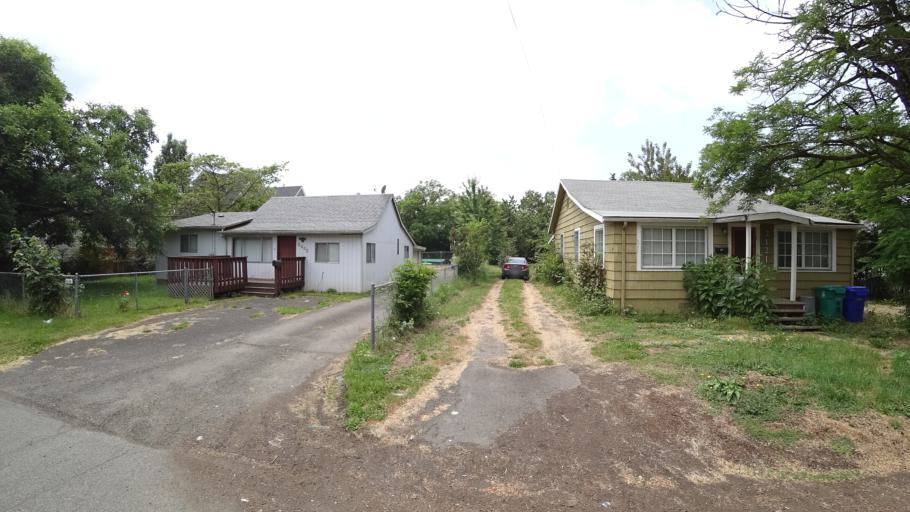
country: US
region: Oregon
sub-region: Multnomah County
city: Lents
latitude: 45.5072
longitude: -122.5723
